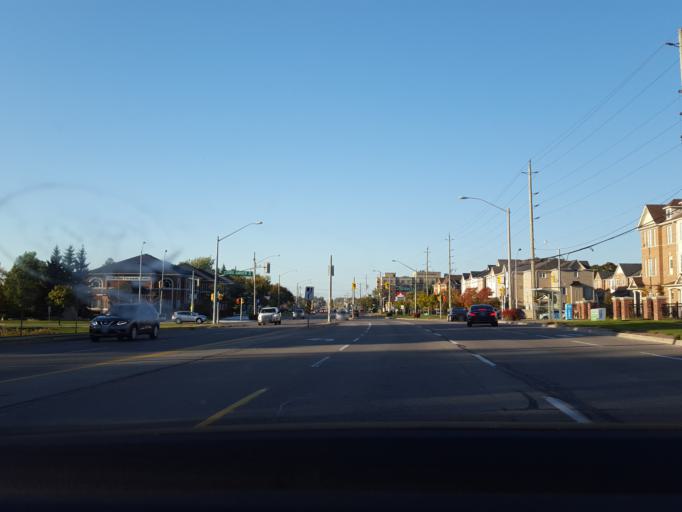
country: CA
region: Ontario
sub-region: York
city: Richmond Hill
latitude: 43.9390
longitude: -79.4534
